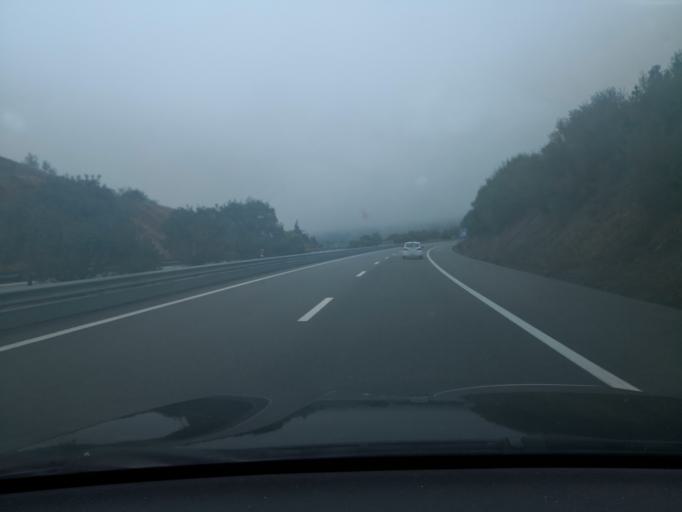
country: PT
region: Braga
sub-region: Celorico de Basto
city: Celorico de Basto
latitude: 41.4481
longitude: -8.0662
